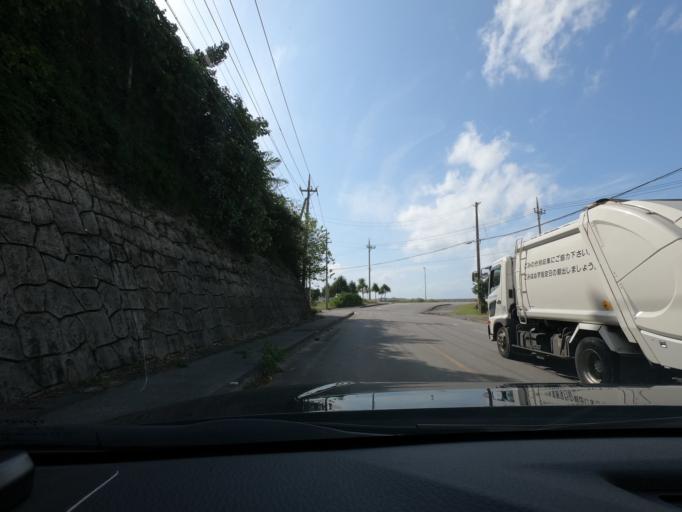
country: JP
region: Okinawa
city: Nago
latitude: 26.7554
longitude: 128.1887
